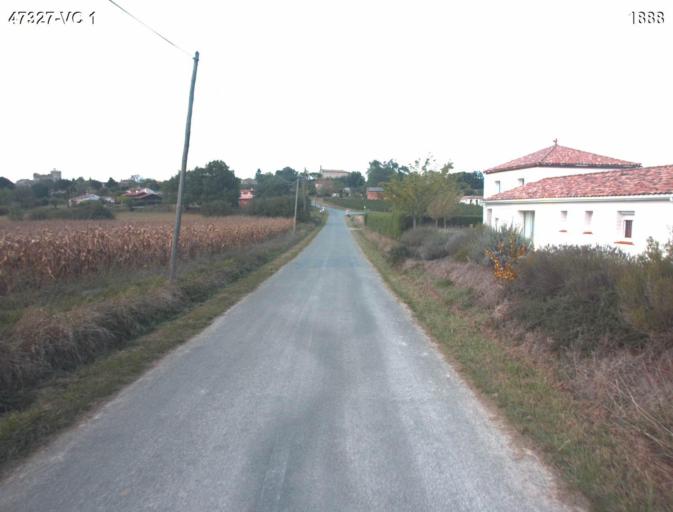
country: FR
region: Aquitaine
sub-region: Departement du Lot-et-Garonne
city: Barbaste
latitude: 44.2014
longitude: 0.2588
